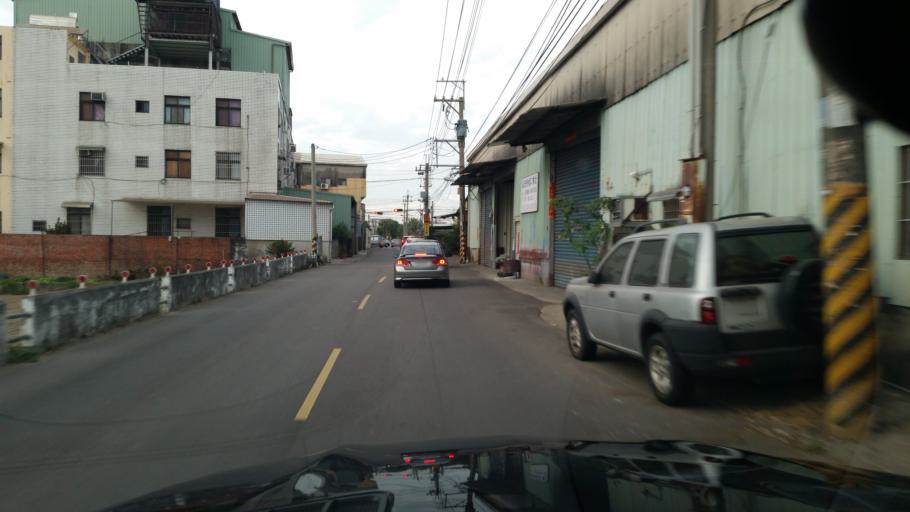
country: TW
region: Taiwan
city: Fengyuan
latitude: 24.2031
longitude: 120.7186
